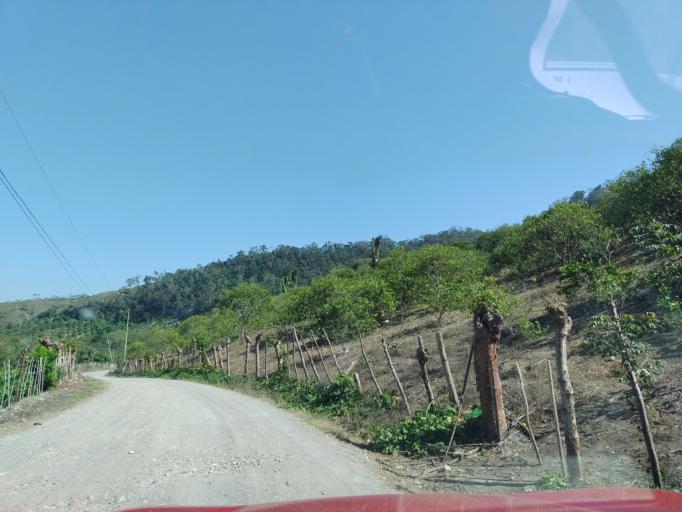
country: MX
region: Veracruz
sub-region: Papantla
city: Polutla
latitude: 20.4834
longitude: -97.1950
